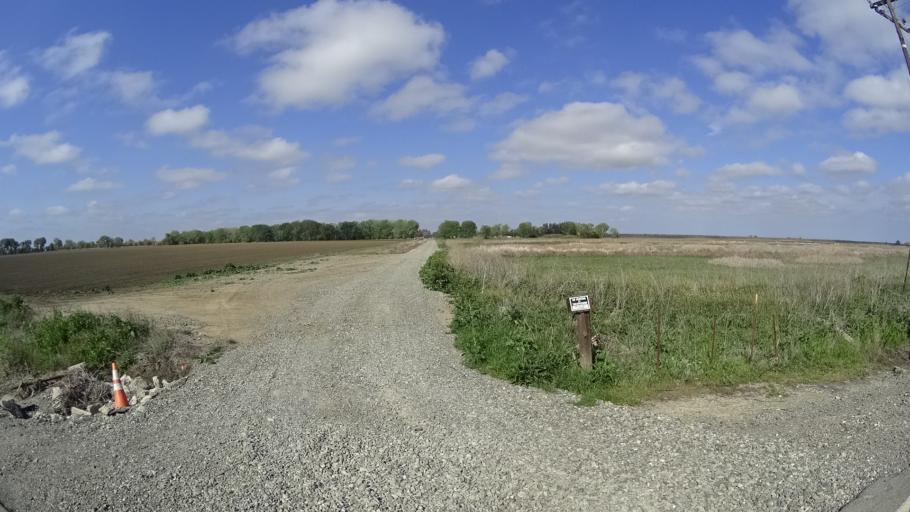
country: US
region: California
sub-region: Colusa County
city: Colusa
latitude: 39.4057
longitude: -121.9292
